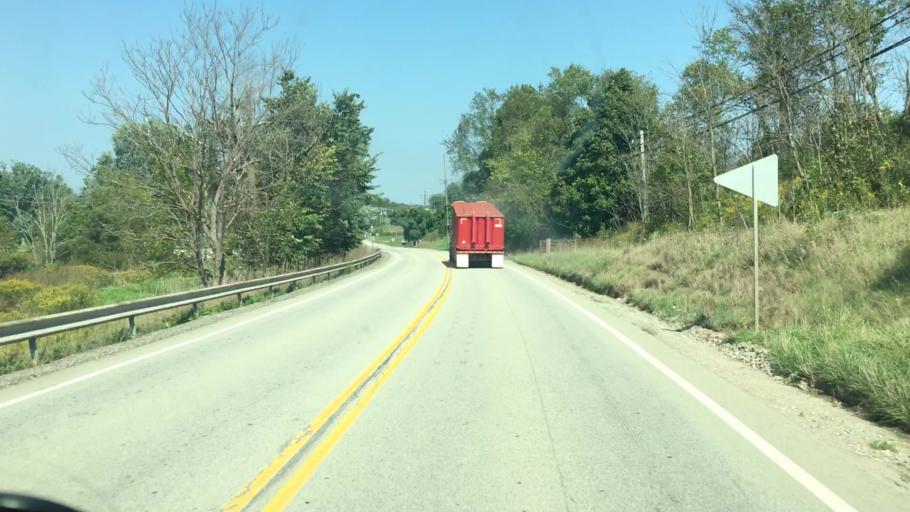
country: US
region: Pennsylvania
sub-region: Washington County
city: Washington
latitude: 40.1184
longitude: -80.2899
